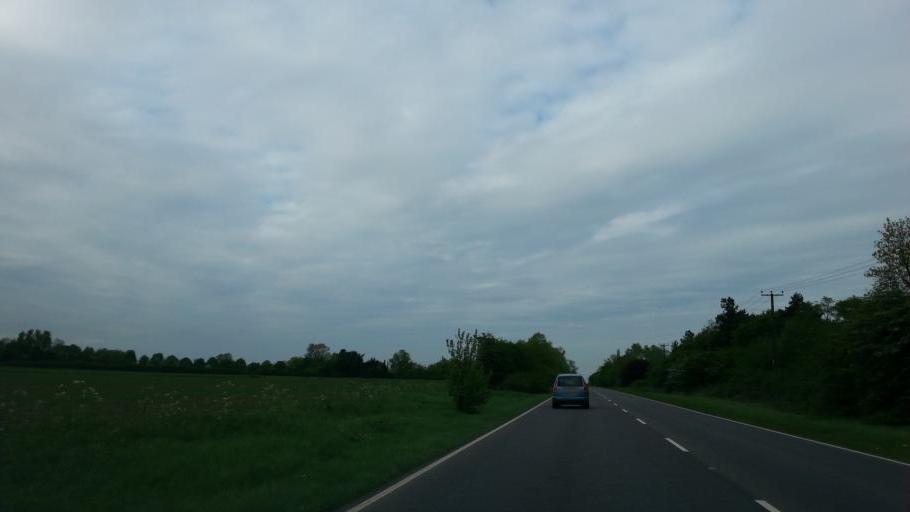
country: GB
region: England
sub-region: Cambridgeshire
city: Doddington
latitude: 52.4912
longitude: 0.0699
